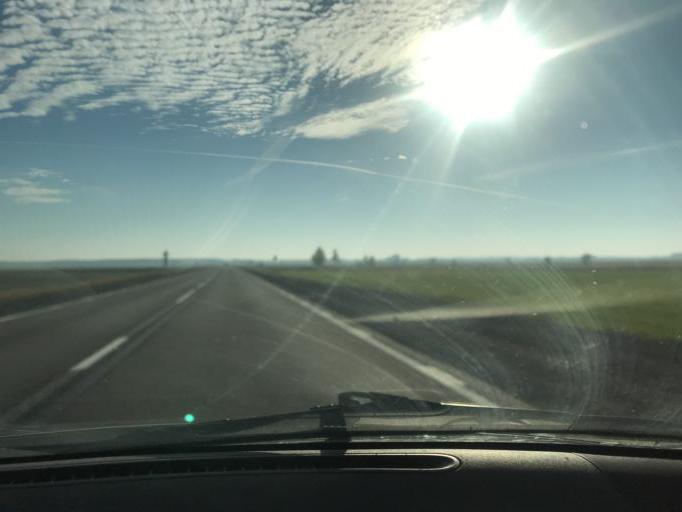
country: BY
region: Brest
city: Drahichyn
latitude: 52.1928
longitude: 25.2547
